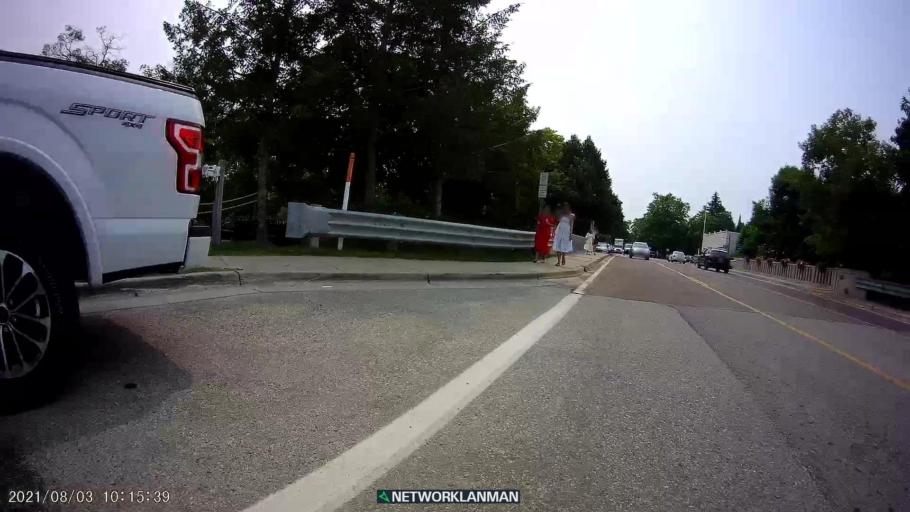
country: US
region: Michigan
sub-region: Leelanau County
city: Leland
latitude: 45.0243
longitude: -85.7593
